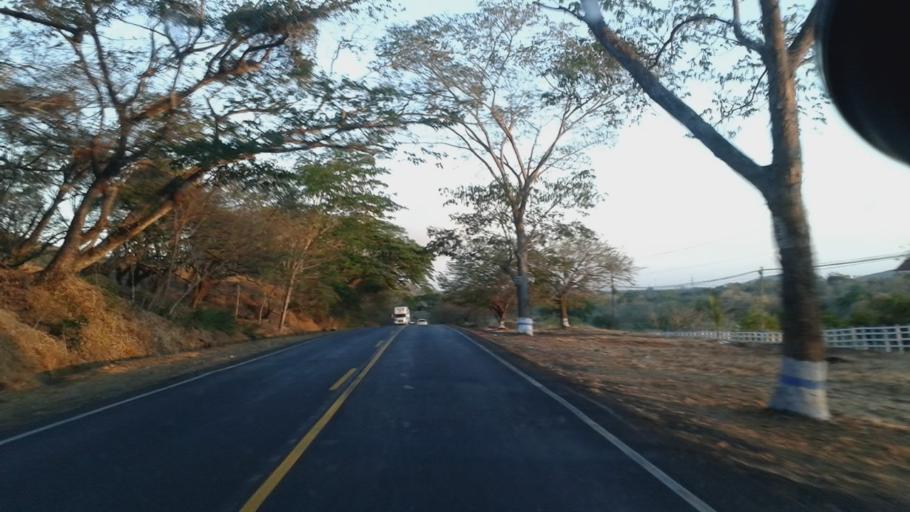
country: CR
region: Guanacaste
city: Juntas
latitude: 10.1428
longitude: -84.9085
